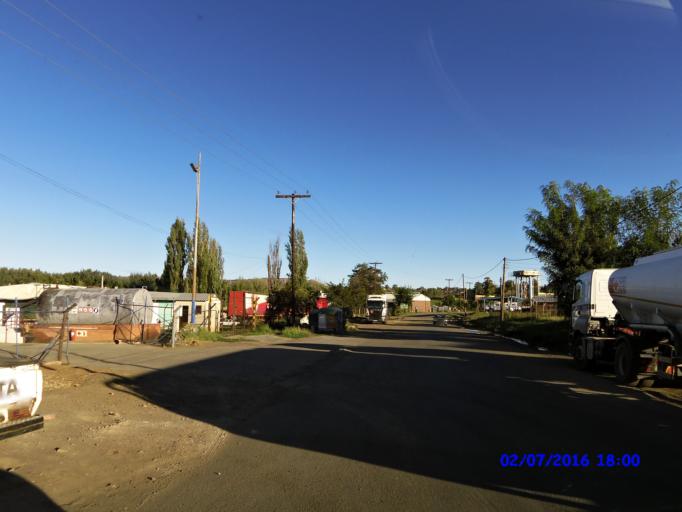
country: LS
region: Maseru
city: Maseru
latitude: -29.2984
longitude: 27.4815
